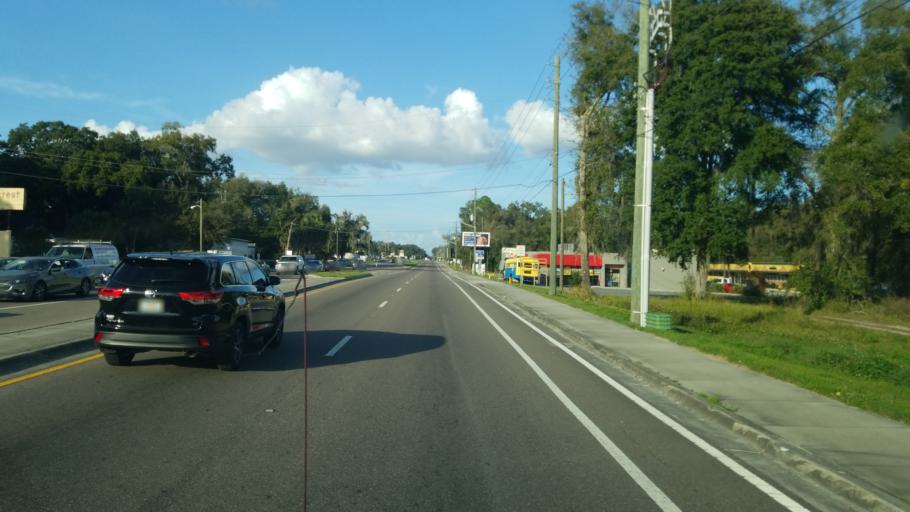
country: US
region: Florida
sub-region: Marion County
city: Ocala
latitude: 29.2155
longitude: -82.1259
